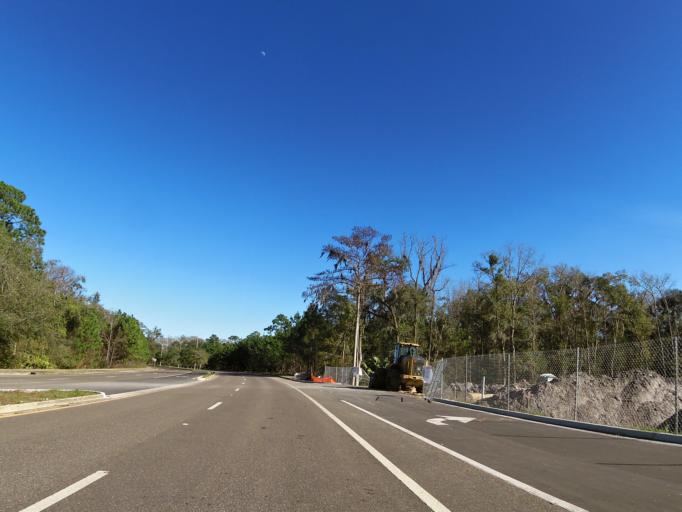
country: US
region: Florida
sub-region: Duval County
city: Jacksonville
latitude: 30.2473
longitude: -81.5679
